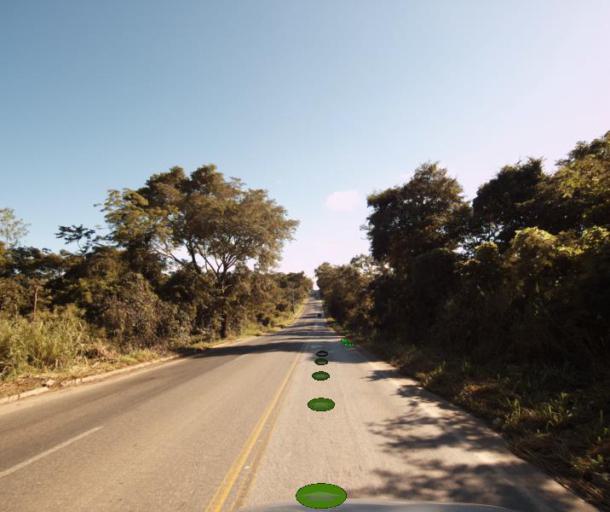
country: BR
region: Goias
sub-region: Uruacu
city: Uruacu
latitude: -14.6035
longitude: -49.1660
